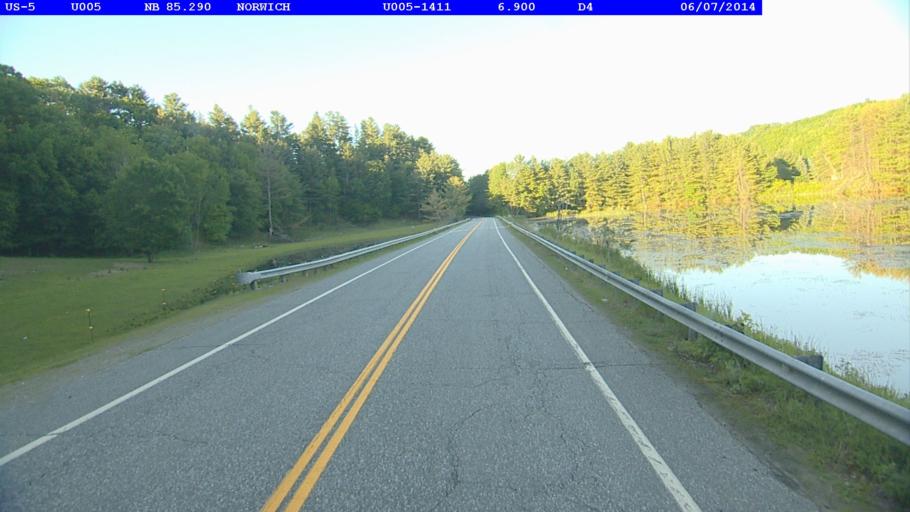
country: US
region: New Hampshire
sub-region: Grafton County
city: Hanover
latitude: 43.7590
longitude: -72.2276
